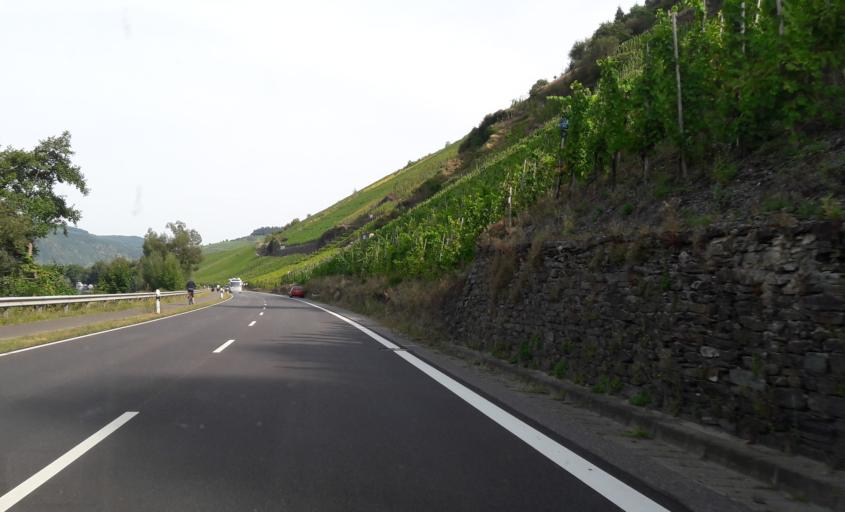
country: DE
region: Rheinland-Pfalz
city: Starkenburg
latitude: 49.9685
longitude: 7.1347
